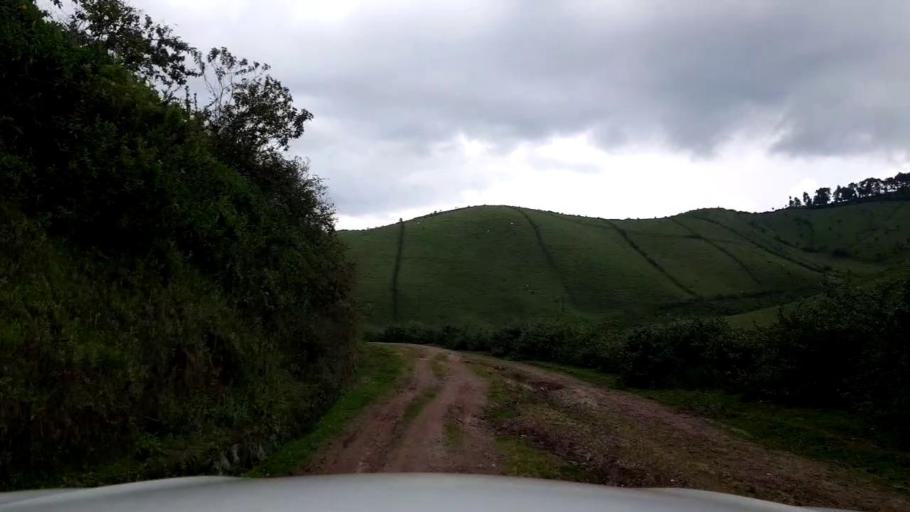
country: RW
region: Western Province
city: Gisenyi
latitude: -1.6800
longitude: 29.4183
